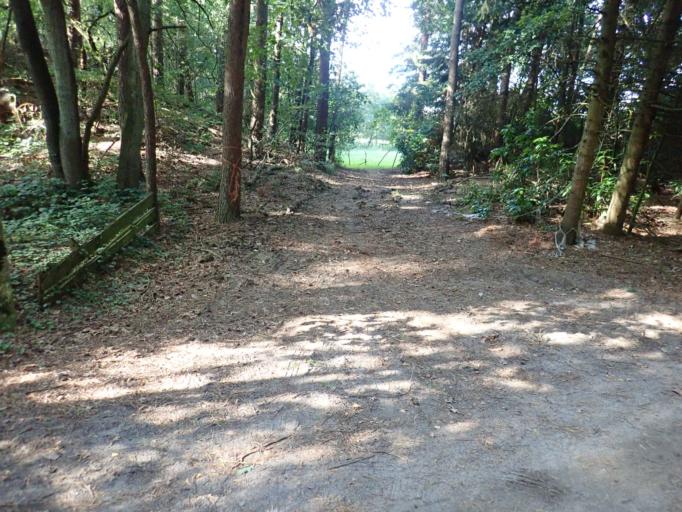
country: BE
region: Flanders
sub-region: Provincie Antwerpen
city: Lille
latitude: 51.2753
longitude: 4.8077
